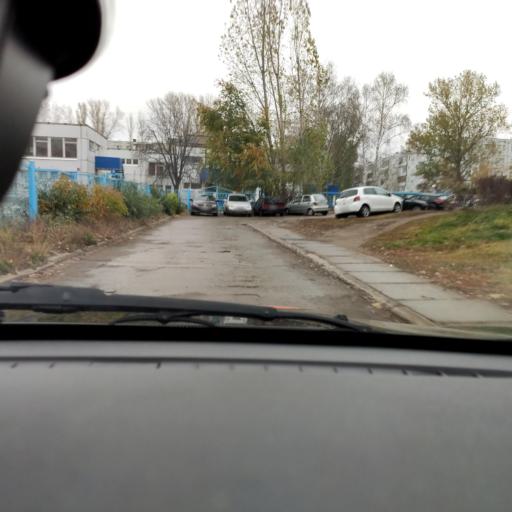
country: RU
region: Samara
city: Tol'yatti
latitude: 53.5295
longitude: 49.2924
